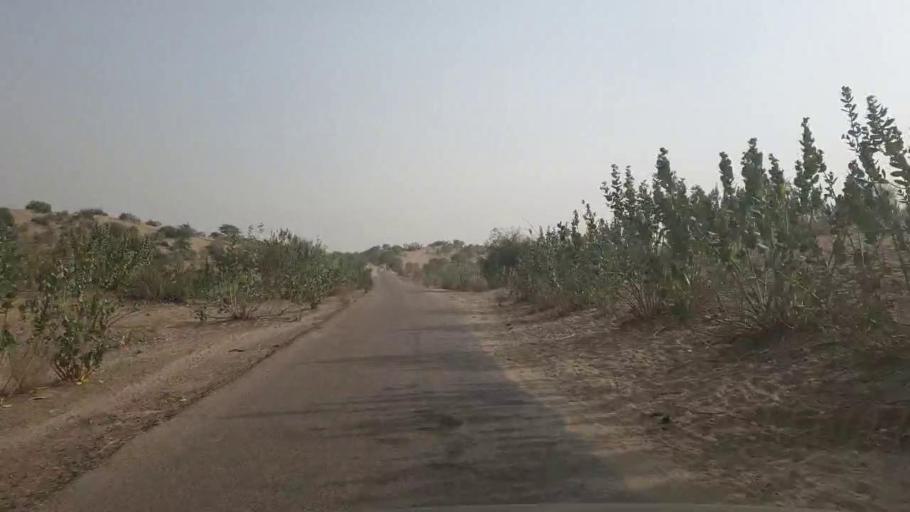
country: PK
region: Sindh
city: Chor
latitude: 25.5313
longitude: 69.9603
